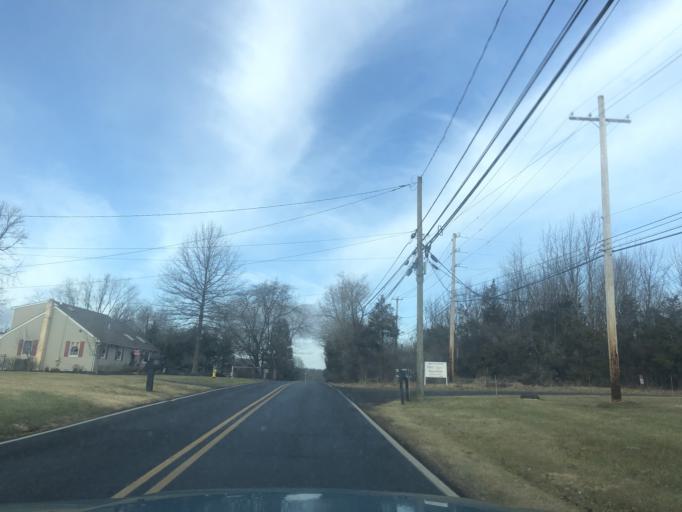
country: US
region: Pennsylvania
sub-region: Bucks County
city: Perkasie
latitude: 40.3780
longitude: -75.3076
